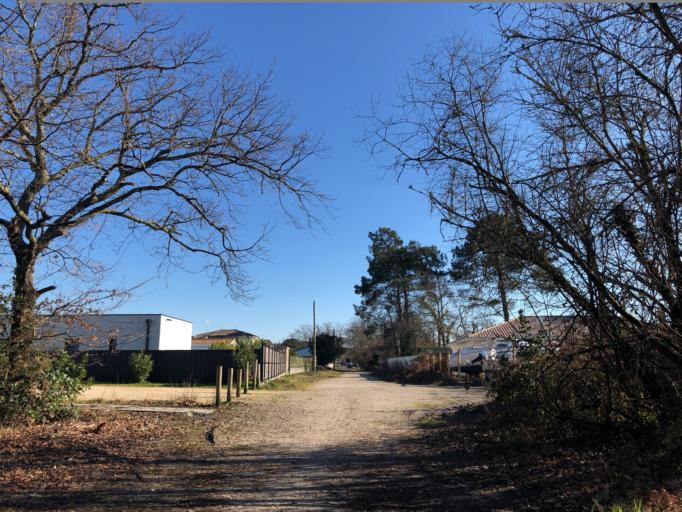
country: FR
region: Aquitaine
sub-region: Departement de la Gironde
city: Andernos-les-Bains
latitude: 44.7506
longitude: -1.0900
